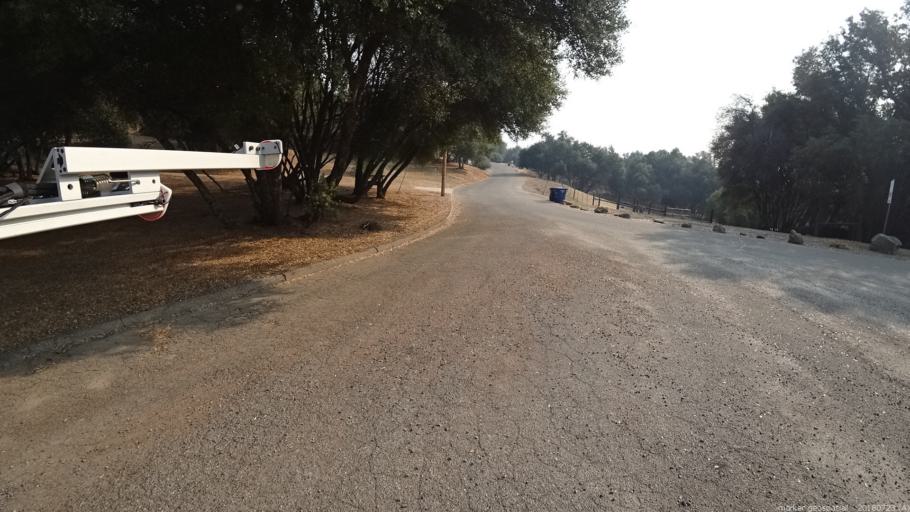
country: US
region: California
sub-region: Madera County
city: Ahwahnee
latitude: 37.3602
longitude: -119.7154
